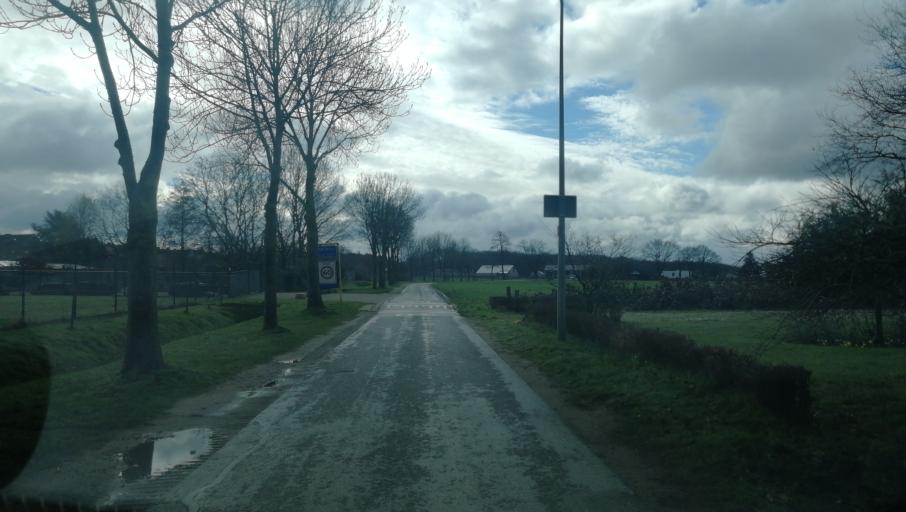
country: NL
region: Limburg
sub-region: Gemeente Venlo
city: Venlo
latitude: 51.4106
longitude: 6.1614
